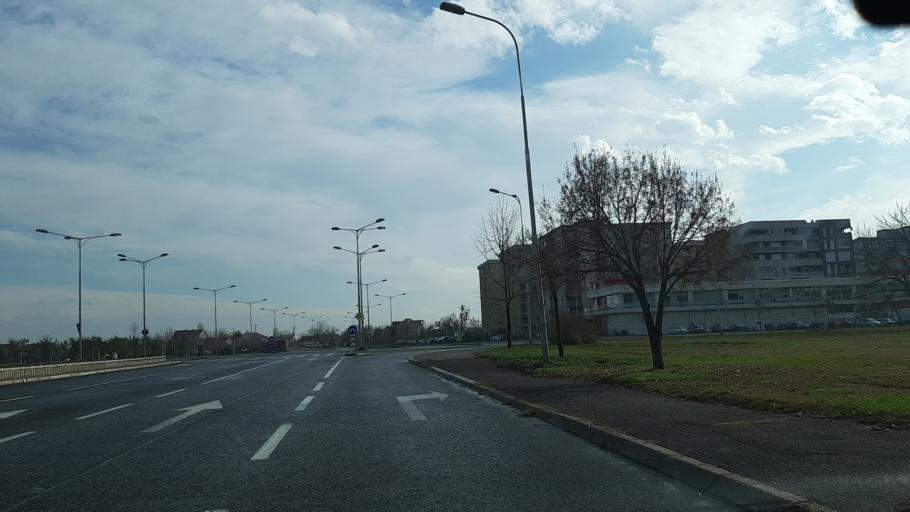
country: MK
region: Kisela Voda
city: Usje
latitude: 41.9856
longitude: 21.4830
